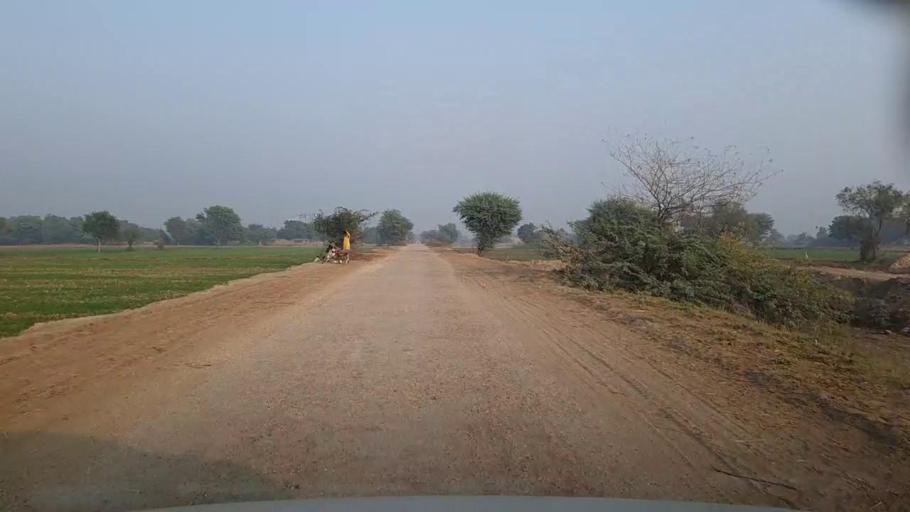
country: PK
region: Sindh
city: Bozdar
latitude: 27.0830
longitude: 68.5497
